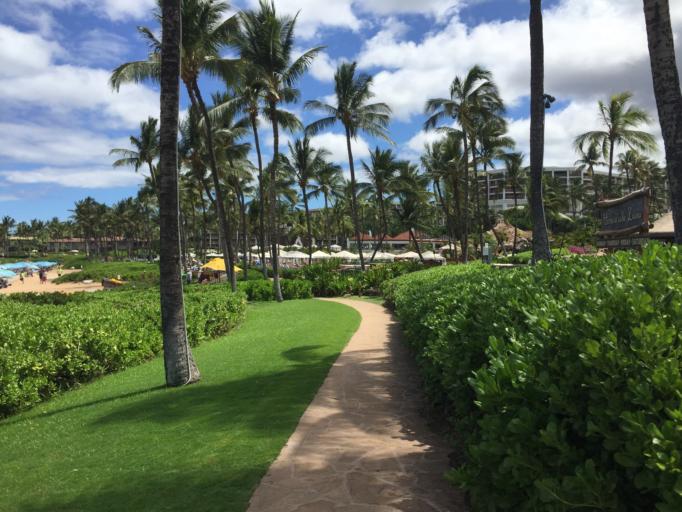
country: US
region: Hawaii
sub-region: Maui County
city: Kihei
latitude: 20.6823
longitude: -156.4428
